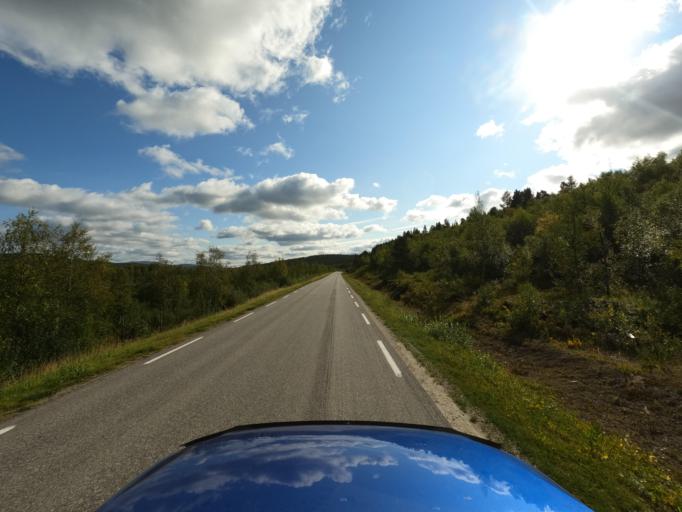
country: NO
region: Finnmark Fylke
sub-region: Karasjok
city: Karasjohka
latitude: 69.4529
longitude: 25.5770
